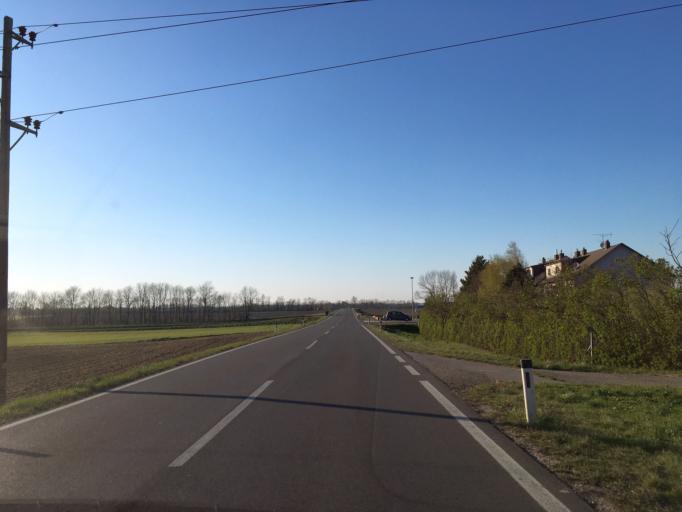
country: AT
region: Lower Austria
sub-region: Politischer Bezirk Tulln
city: Konigstetten
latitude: 48.3017
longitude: 16.1388
